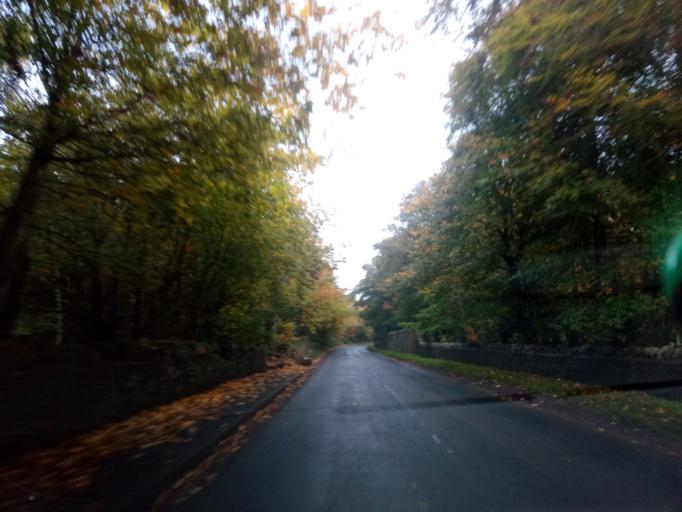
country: GB
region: Scotland
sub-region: The Scottish Borders
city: Eyemouth
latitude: 55.8455
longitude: -2.1193
